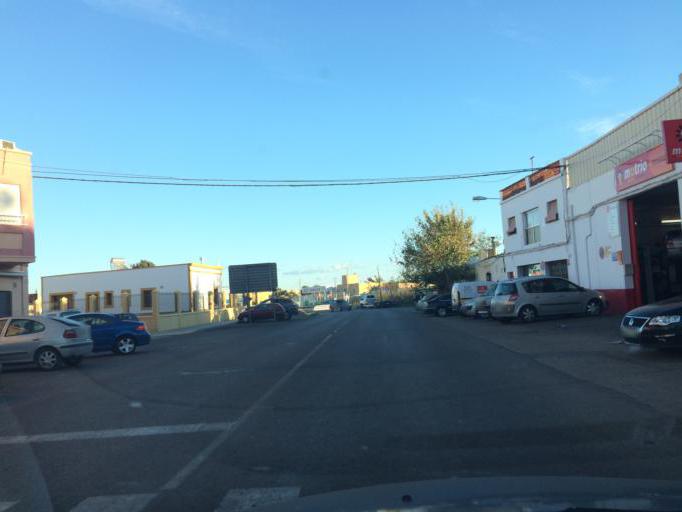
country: ES
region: Andalusia
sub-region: Provincia de Almeria
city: Almeria
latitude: 36.8414
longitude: -2.4253
